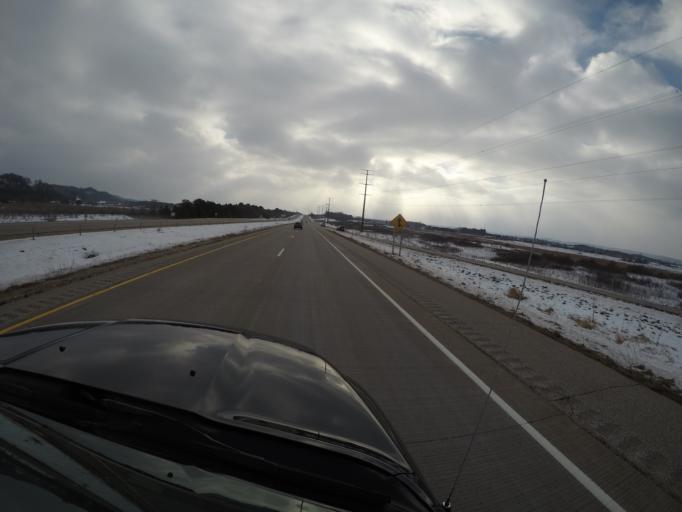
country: US
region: Wisconsin
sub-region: La Crosse County
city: Holmen
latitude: 43.9946
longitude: -91.2864
